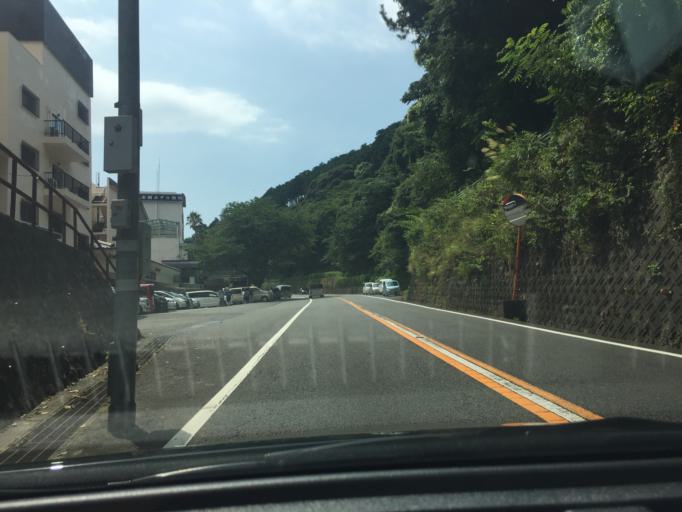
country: JP
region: Shizuoka
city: Ito
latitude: 34.8151
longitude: 139.0677
